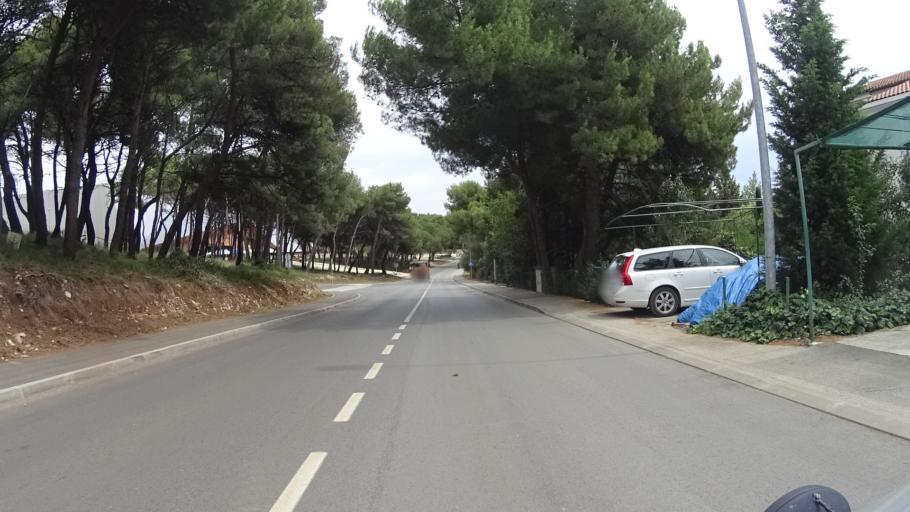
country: HR
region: Istarska
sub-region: Grad Pula
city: Pula
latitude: 44.8608
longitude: 13.8213
